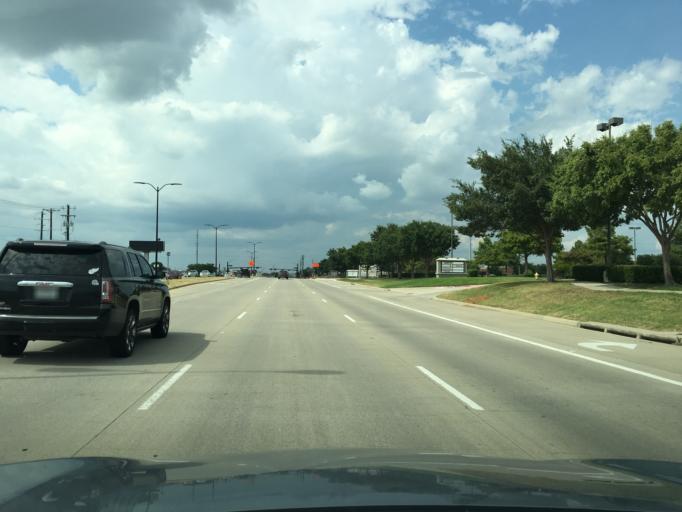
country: US
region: Texas
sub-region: Denton County
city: Little Elm
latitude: 33.1502
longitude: -96.8908
